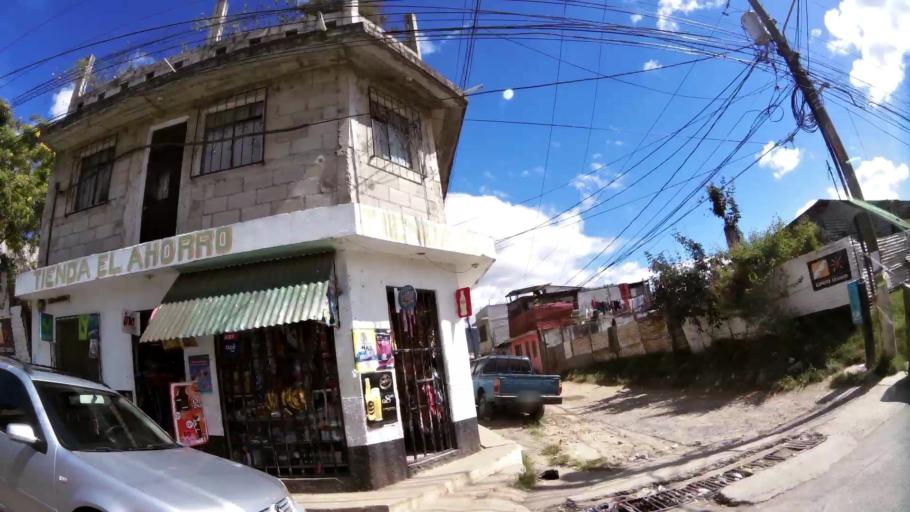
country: GT
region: Guatemala
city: Petapa
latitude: 14.5451
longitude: -90.5461
